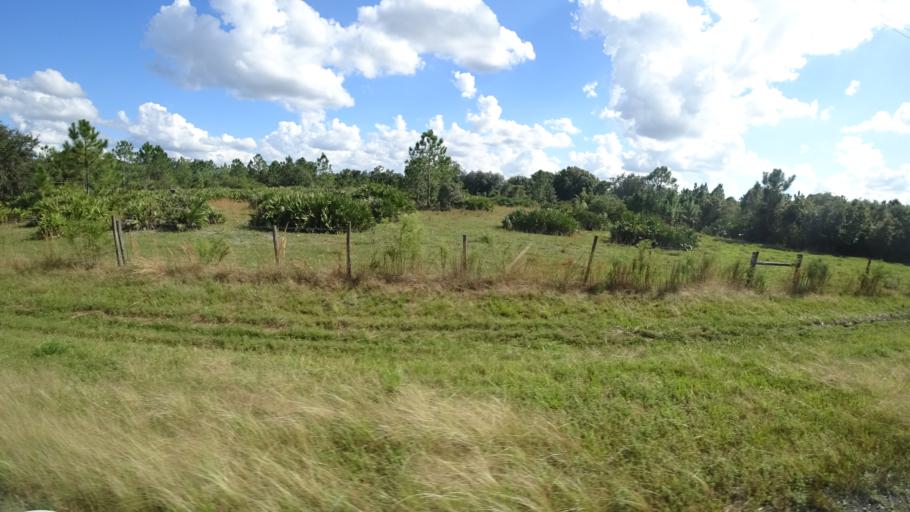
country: US
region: Florida
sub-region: Hardee County
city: Wauchula
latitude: 27.4534
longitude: -82.0978
